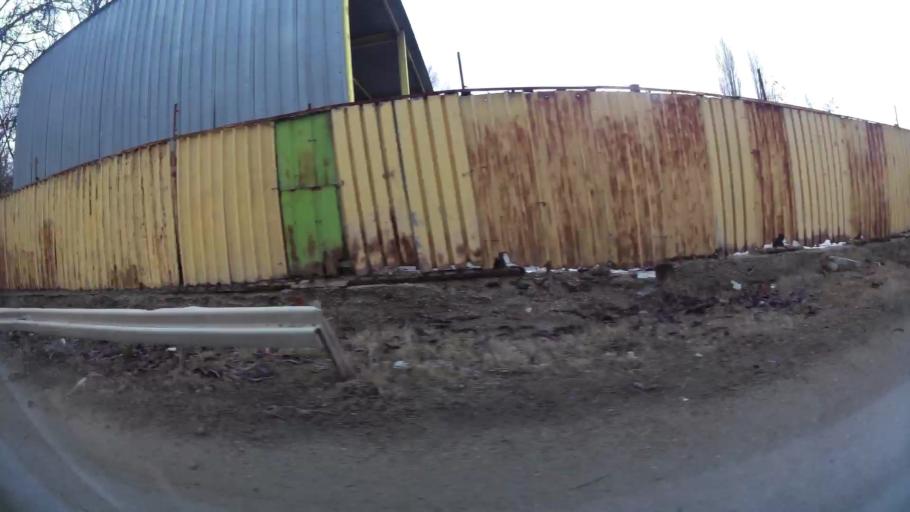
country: BG
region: Sofia-Capital
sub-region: Stolichna Obshtina
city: Sofia
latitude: 42.6659
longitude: 23.2484
